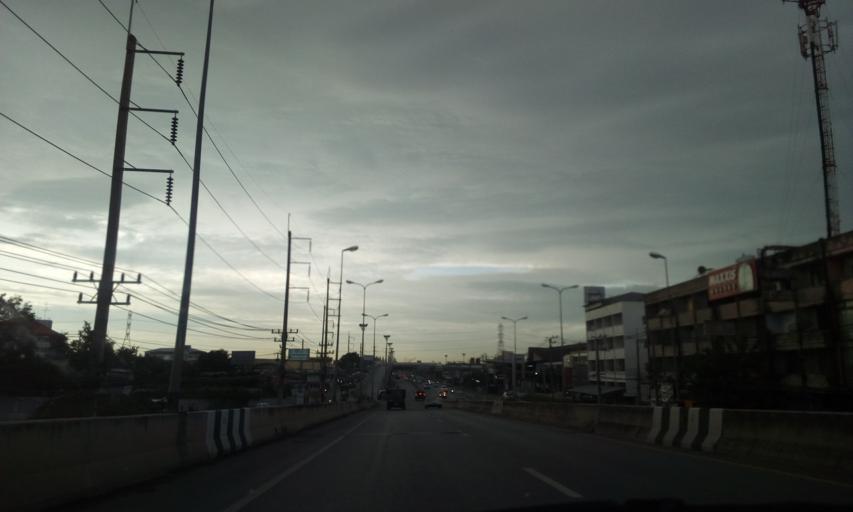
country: TH
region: Phra Nakhon Si Ayutthaya
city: Ban Bang Kadi Pathum Thani
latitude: 13.9692
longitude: 100.5506
